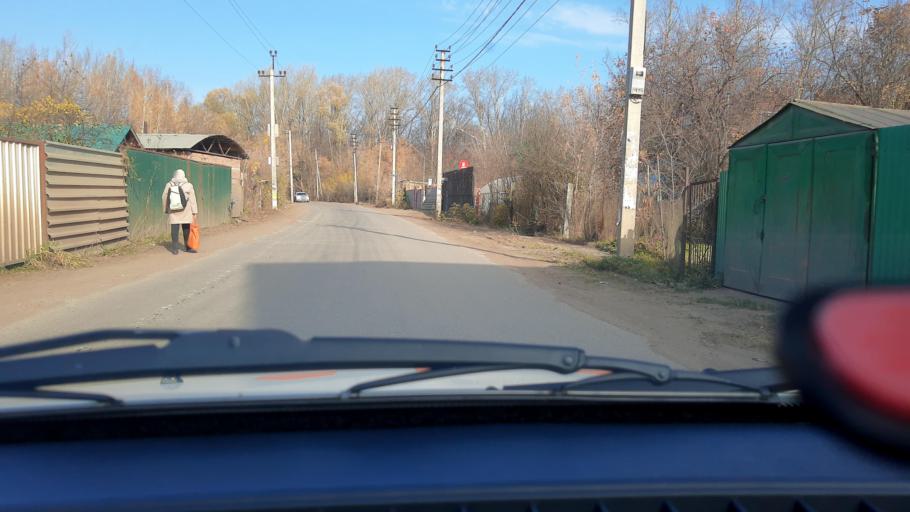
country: RU
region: Bashkortostan
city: Ufa
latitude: 54.6957
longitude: 55.9023
